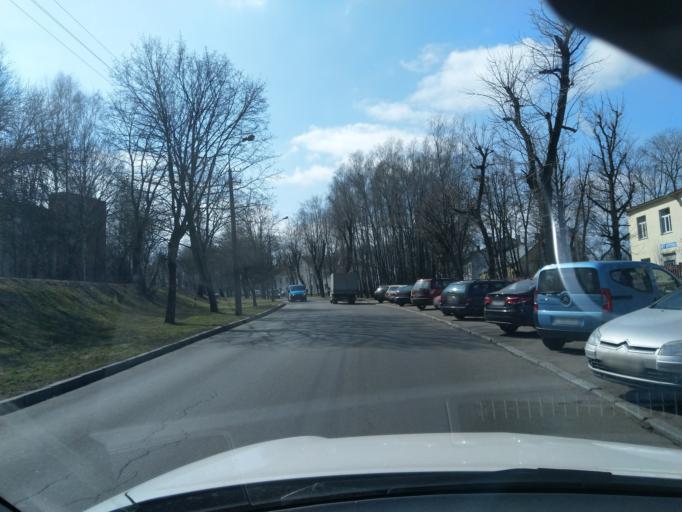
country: BY
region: Minsk
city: Syenitsa
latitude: 53.8756
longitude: 27.5122
